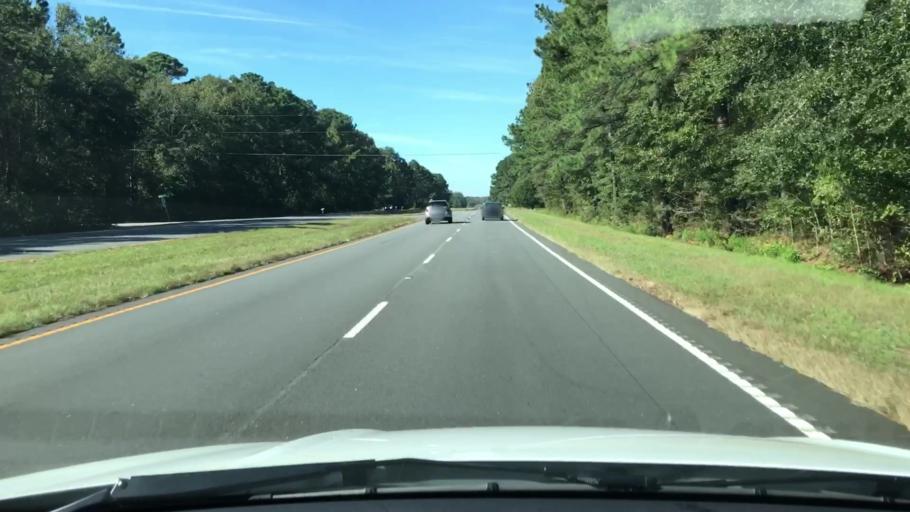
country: US
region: South Carolina
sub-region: Hampton County
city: Yemassee
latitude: 32.5909
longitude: -80.7487
